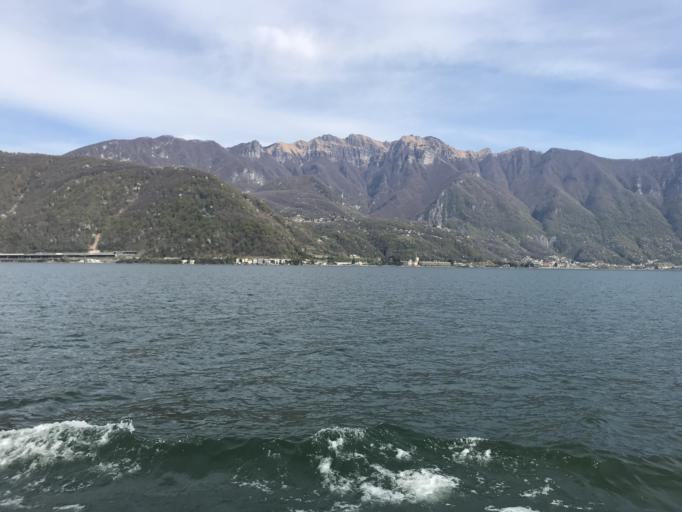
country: CH
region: Ticino
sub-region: Lugano District
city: Melide
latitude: 45.9408
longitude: 8.9444
